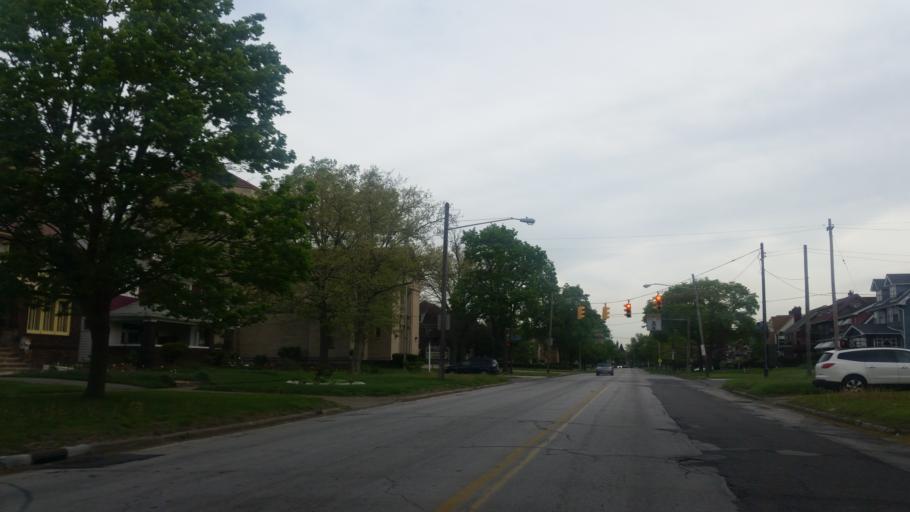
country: US
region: Ohio
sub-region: Cuyahoga County
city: Newburgh Heights
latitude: 41.4775
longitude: -81.6097
